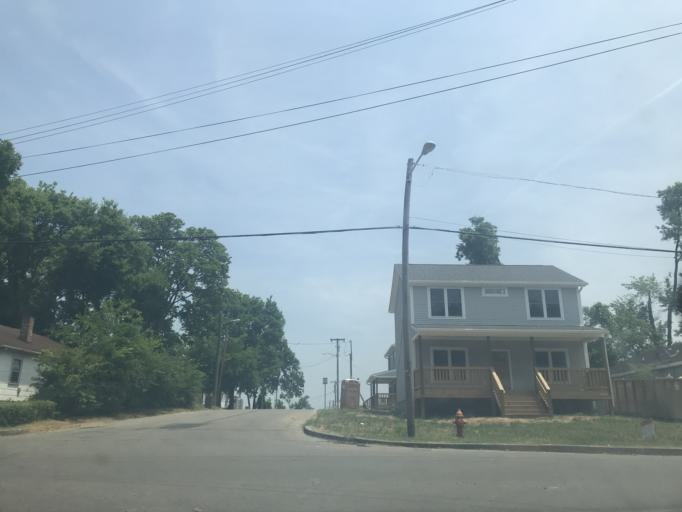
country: US
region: Tennessee
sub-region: Davidson County
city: Nashville
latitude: 36.1890
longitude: -86.8108
